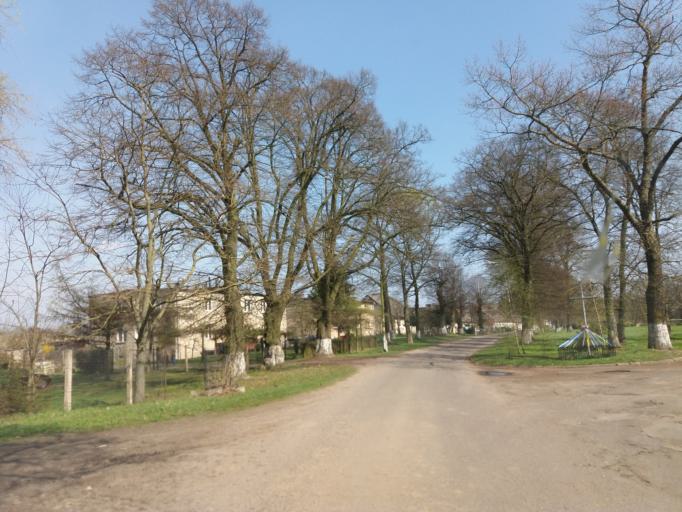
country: PL
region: West Pomeranian Voivodeship
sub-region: Powiat choszczenski
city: Recz
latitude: 53.2630
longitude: 15.6131
